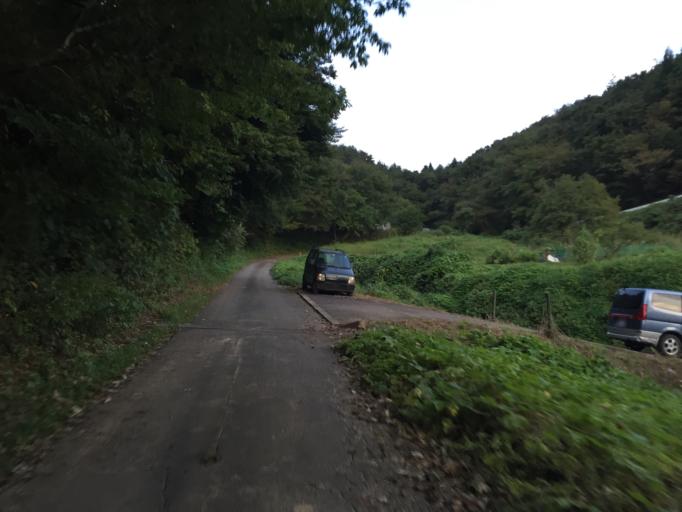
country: JP
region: Fukushima
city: Fukushima-shi
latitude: 37.7338
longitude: 140.4896
